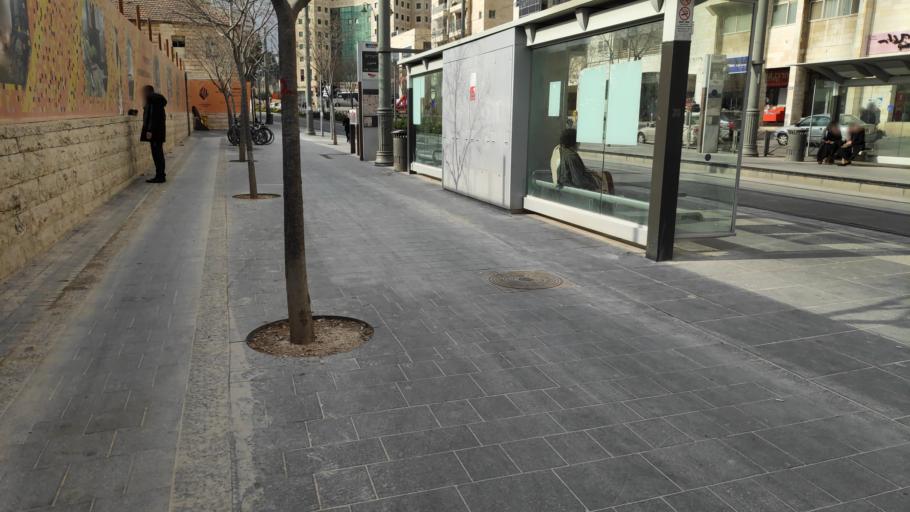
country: IL
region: Jerusalem
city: West Jerusalem
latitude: 31.7878
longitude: 35.2069
